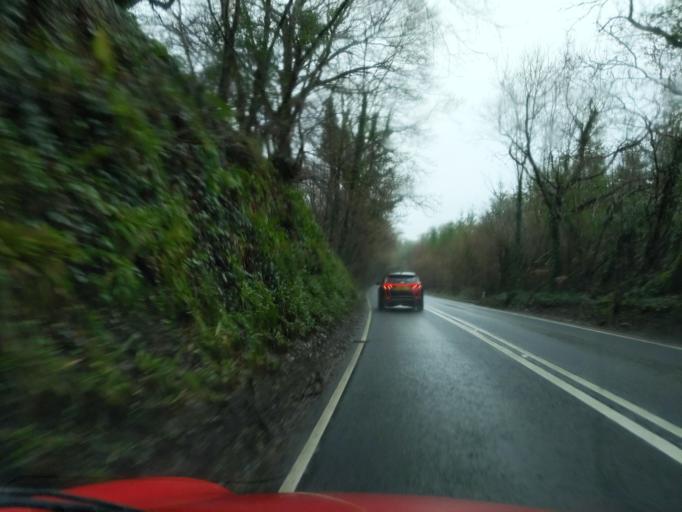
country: GB
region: England
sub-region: Cornwall
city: Launceston
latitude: 50.5894
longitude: -4.3331
